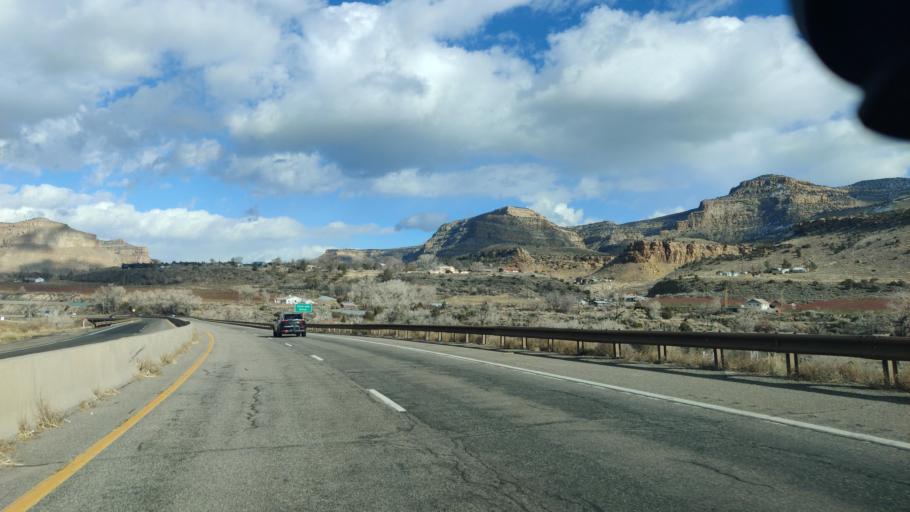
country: US
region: Colorado
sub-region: Mesa County
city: Palisade
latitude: 39.1205
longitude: -108.3240
